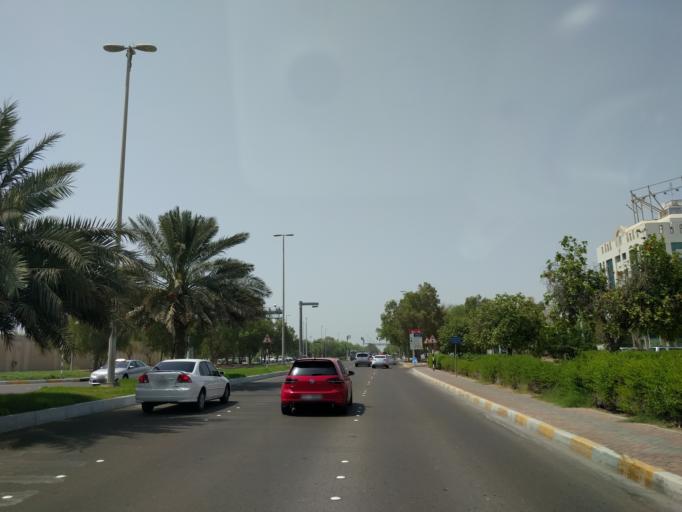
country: AE
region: Abu Dhabi
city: Abu Dhabi
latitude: 24.4323
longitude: 54.4298
